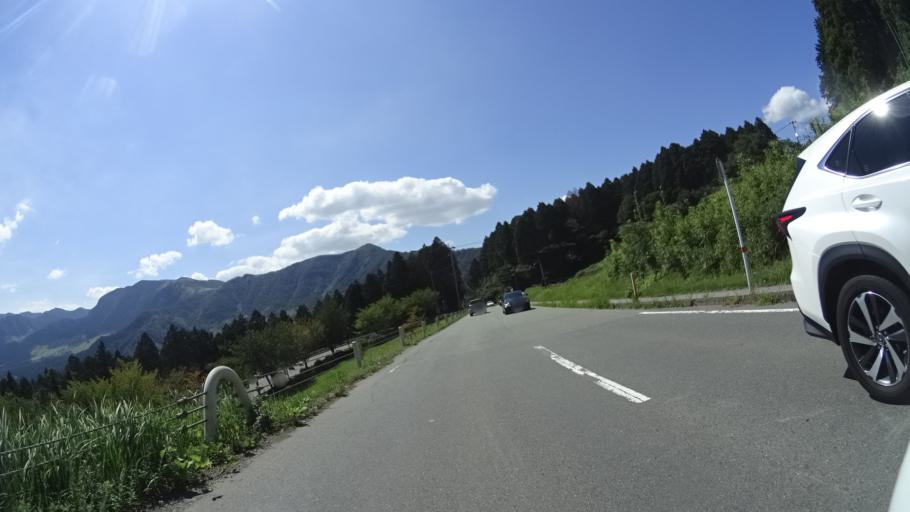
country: JP
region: Kumamoto
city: Aso
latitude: 32.8718
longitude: 131.0037
